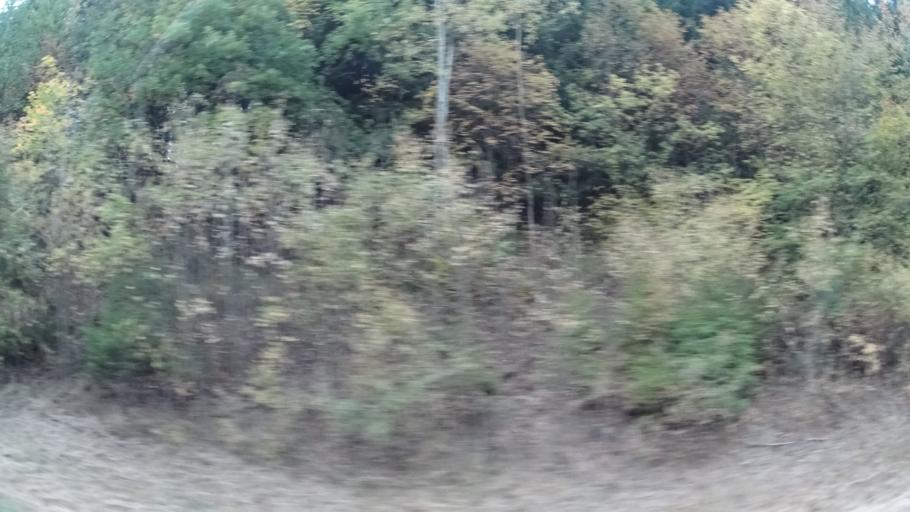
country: DE
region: Hesse
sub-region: Regierungsbezirk Kassel
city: Poppenhausen
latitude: 50.5273
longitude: 9.9102
